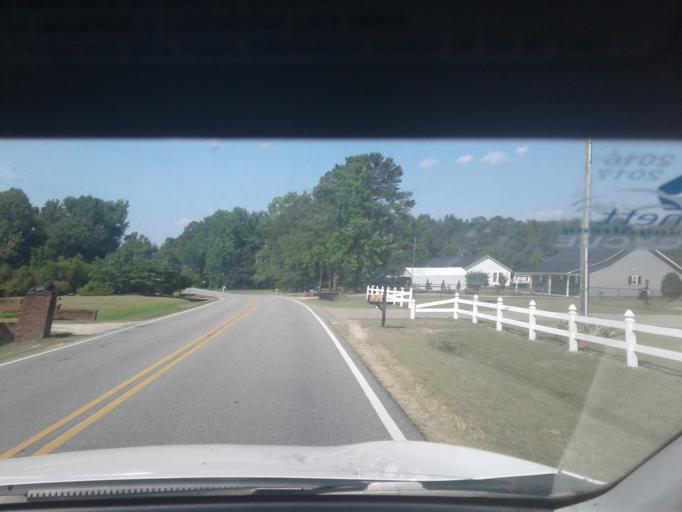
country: US
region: North Carolina
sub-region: Johnston County
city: Benson
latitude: 35.3954
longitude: -78.6027
